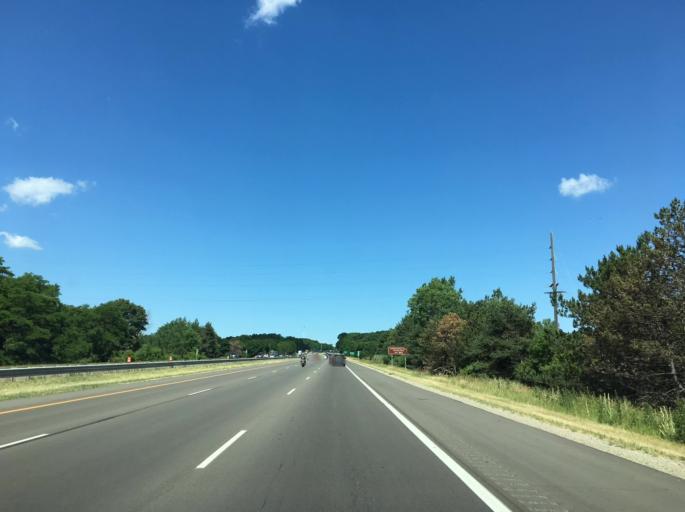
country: US
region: Michigan
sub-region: Oakland County
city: Clarkston
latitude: 42.7272
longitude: -83.3590
